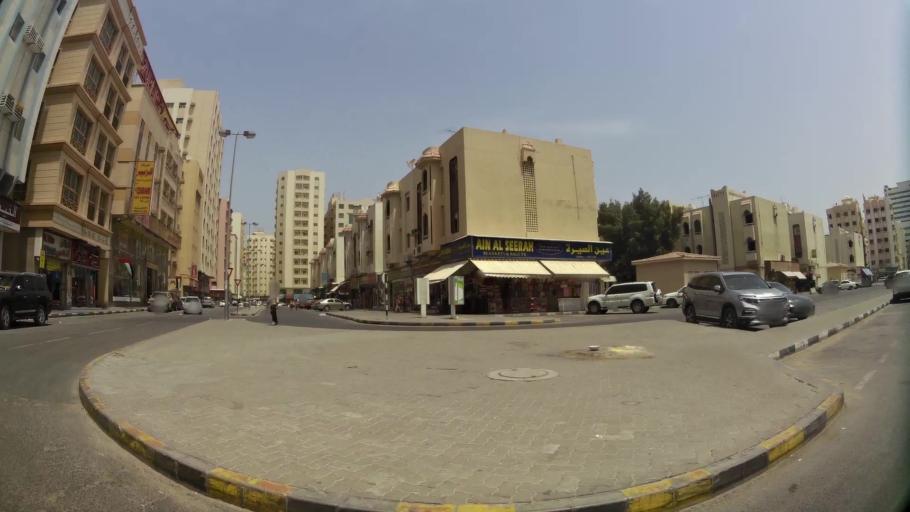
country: AE
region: Ash Shariqah
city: Sharjah
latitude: 25.3574
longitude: 55.3925
